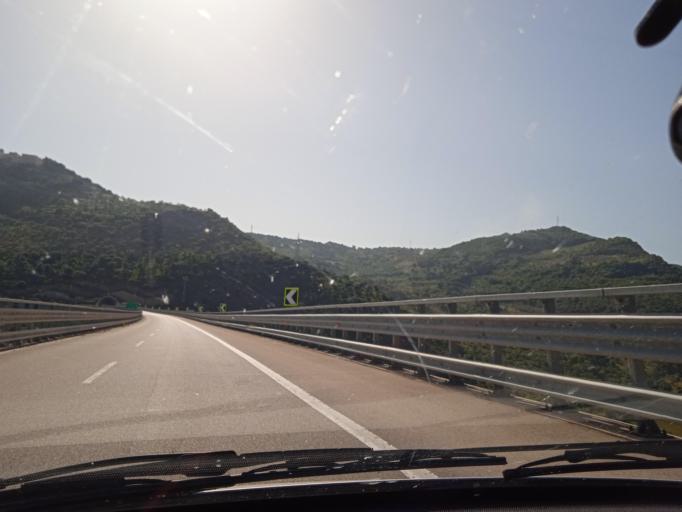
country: IT
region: Sicily
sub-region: Messina
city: Caronia
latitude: 38.0190
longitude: 14.4321
